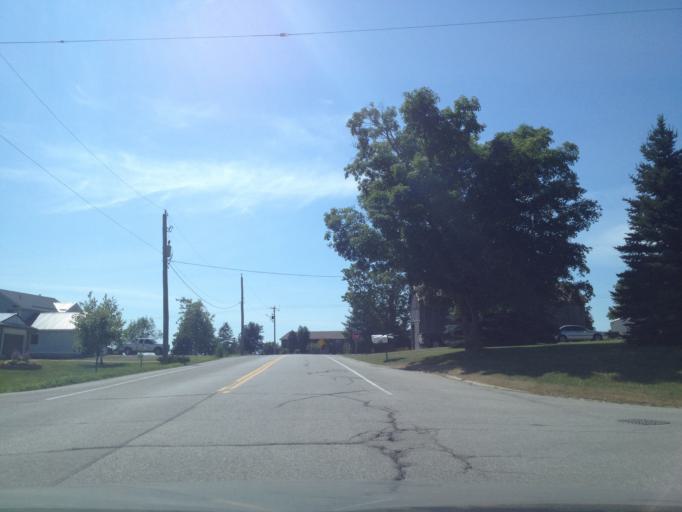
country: CA
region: Ontario
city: Waterloo
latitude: 43.5278
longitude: -80.7422
